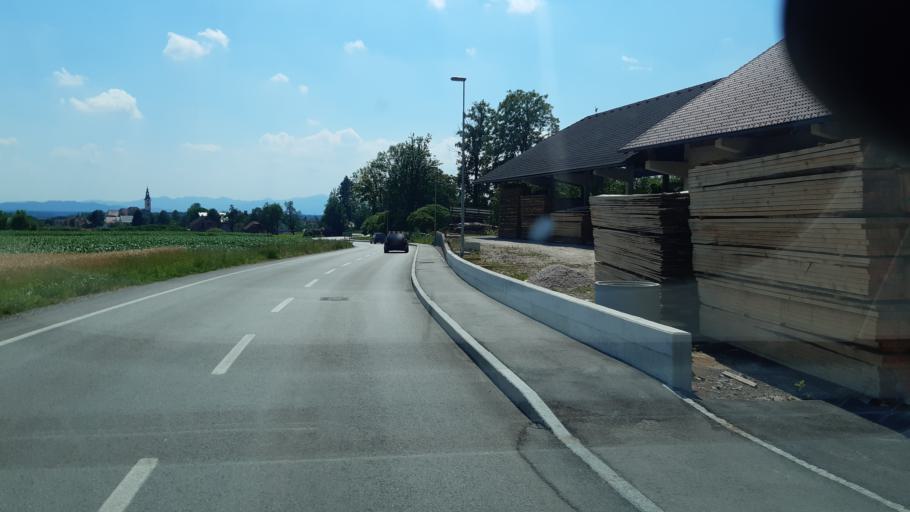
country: SI
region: Cerklje na Gorenjskem
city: Cerklje na Gorenjskem
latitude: 46.2602
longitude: 14.4916
